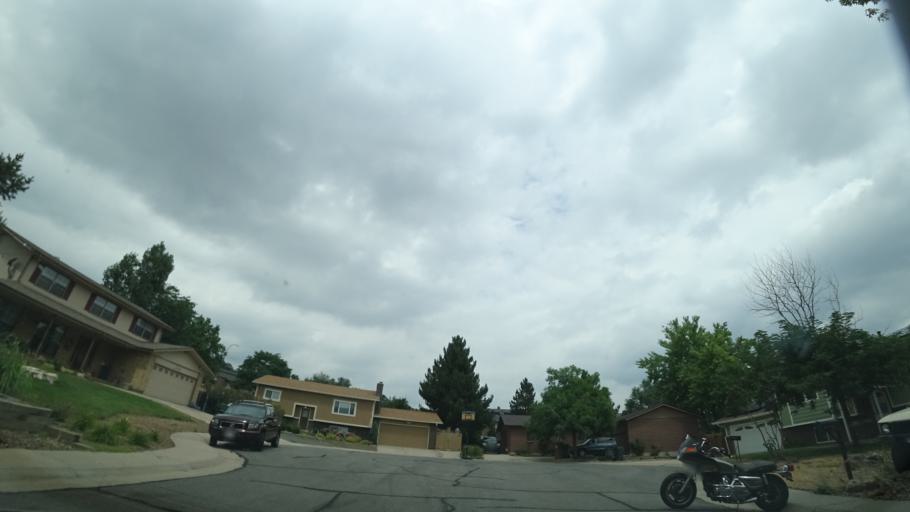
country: US
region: Colorado
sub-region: Jefferson County
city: West Pleasant View
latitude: 39.7170
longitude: -105.1450
